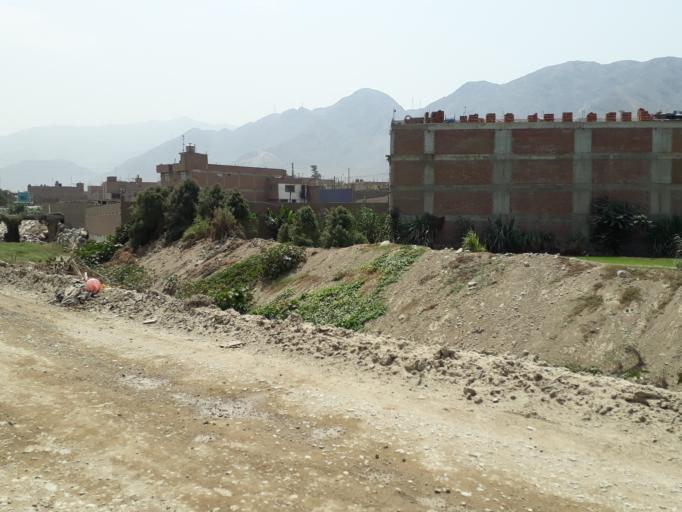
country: PE
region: Lima
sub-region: Lima
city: Santa Maria
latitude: -11.9906
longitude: -76.9037
